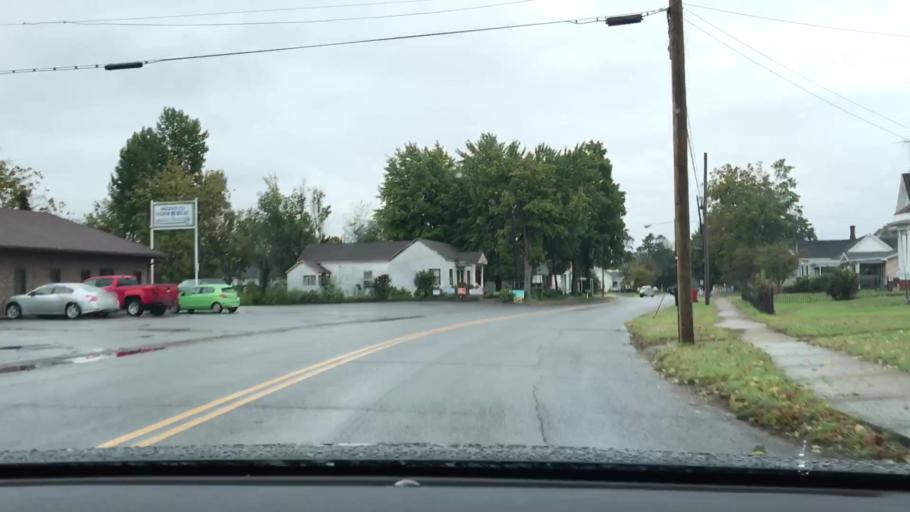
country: US
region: Kentucky
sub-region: McLean County
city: Calhoun
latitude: 37.5419
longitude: -87.2586
